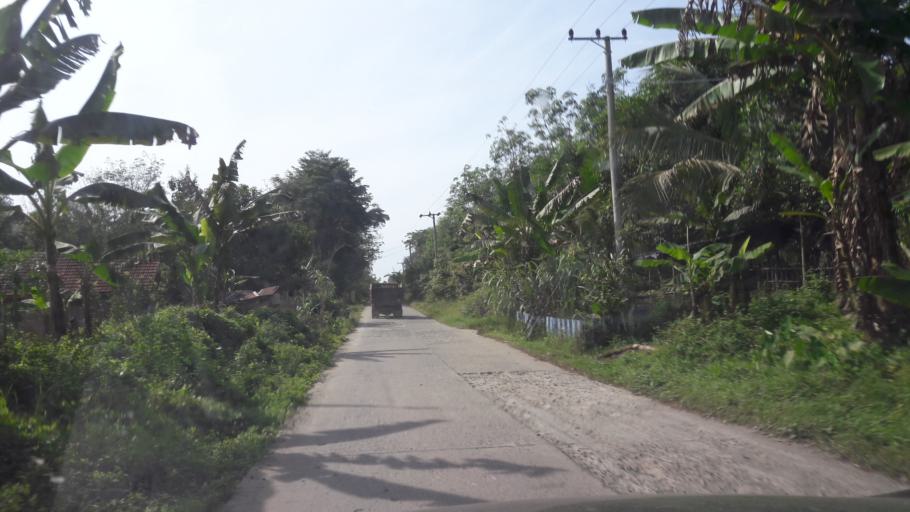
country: ID
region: South Sumatra
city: Gunungmenang
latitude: -3.3325
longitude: 104.0639
